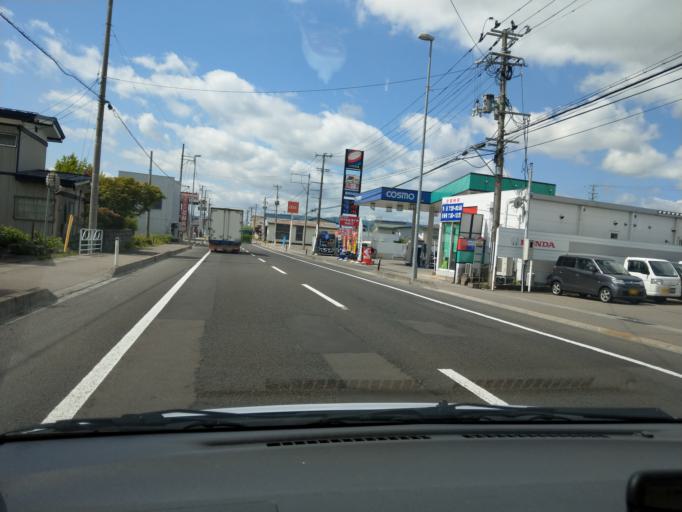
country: JP
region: Akita
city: Yuzawa
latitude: 39.1756
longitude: 140.4924
